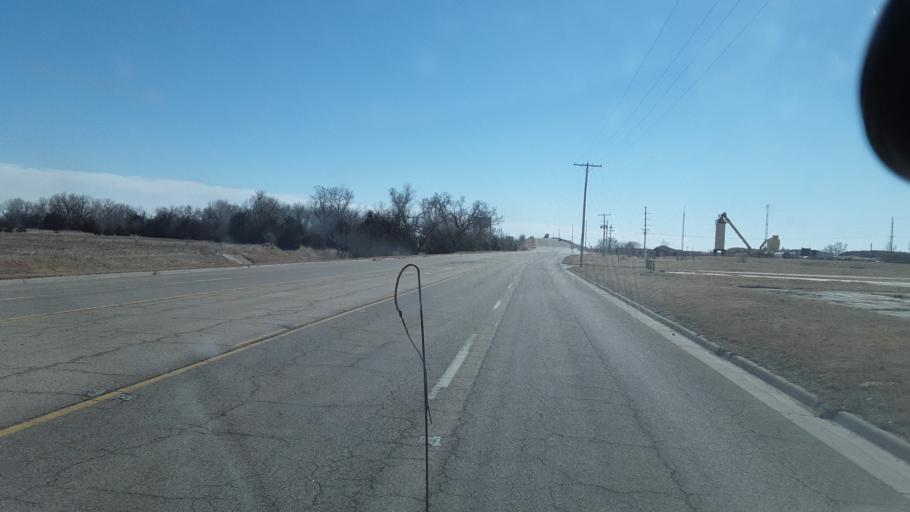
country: US
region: Kansas
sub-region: Reno County
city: Hutchinson
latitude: 38.0540
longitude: -97.8670
